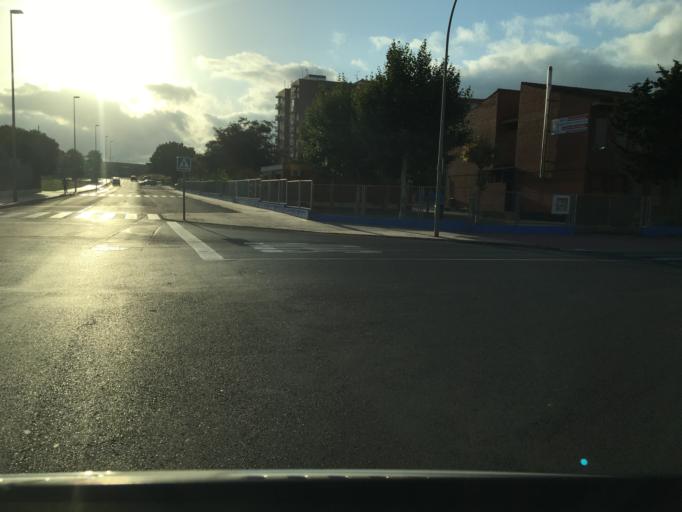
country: ES
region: Murcia
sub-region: Murcia
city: Cartagena
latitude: 37.6189
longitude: -0.9925
